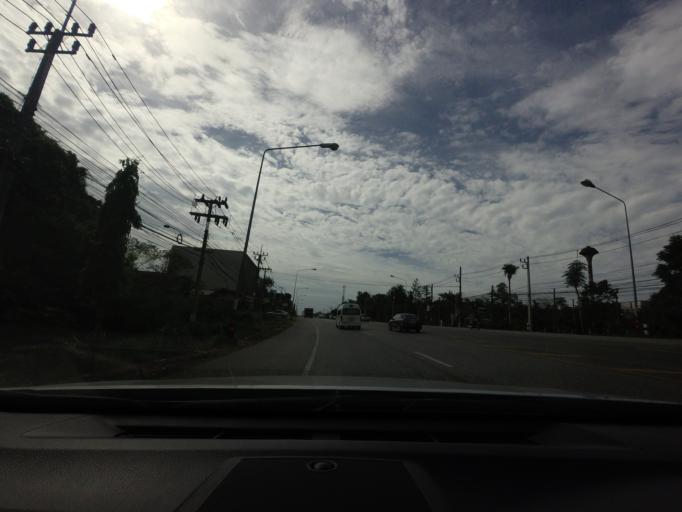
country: TH
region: Songkhla
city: Hat Yai
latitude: 6.9715
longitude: 100.4293
